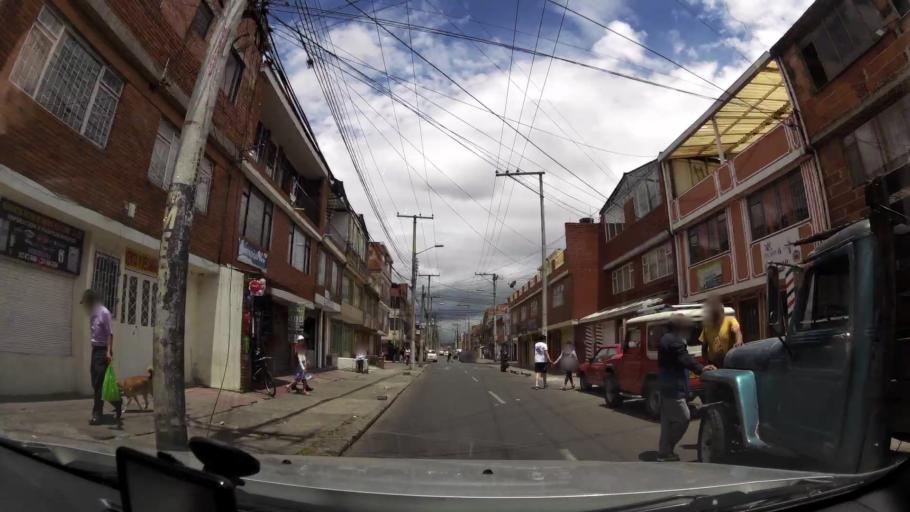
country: CO
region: Bogota D.C.
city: Bogota
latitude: 4.6102
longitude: -74.1128
